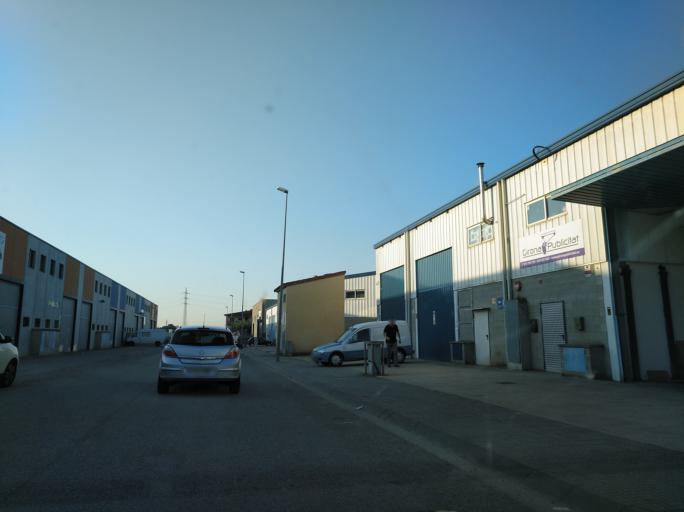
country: ES
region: Catalonia
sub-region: Provincia de Girona
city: Vilablareix
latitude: 41.9653
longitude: 2.7764
